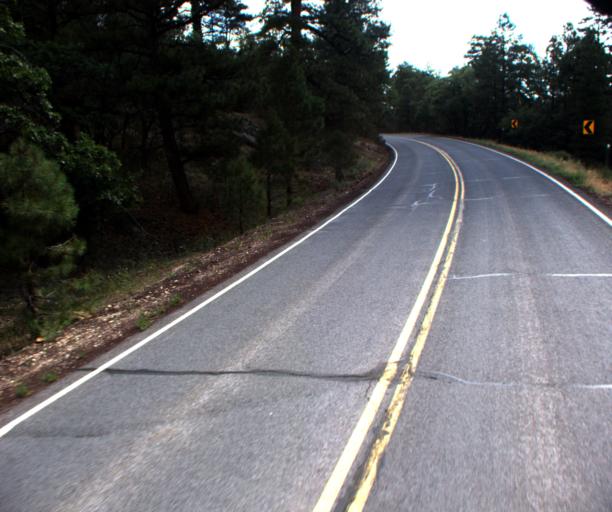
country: US
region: Arizona
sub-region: Coconino County
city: Grand Canyon
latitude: 35.9802
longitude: -111.9470
